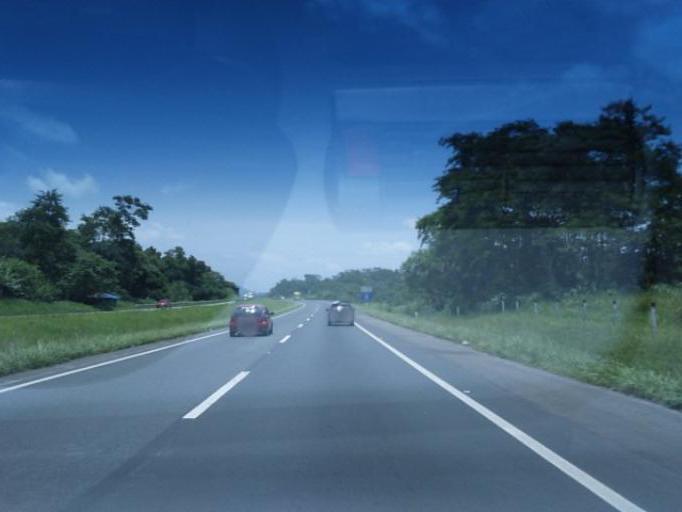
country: BR
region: Sao Paulo
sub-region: Miracatu
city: Miracatu
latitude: -24.2649
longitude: -47.3869
